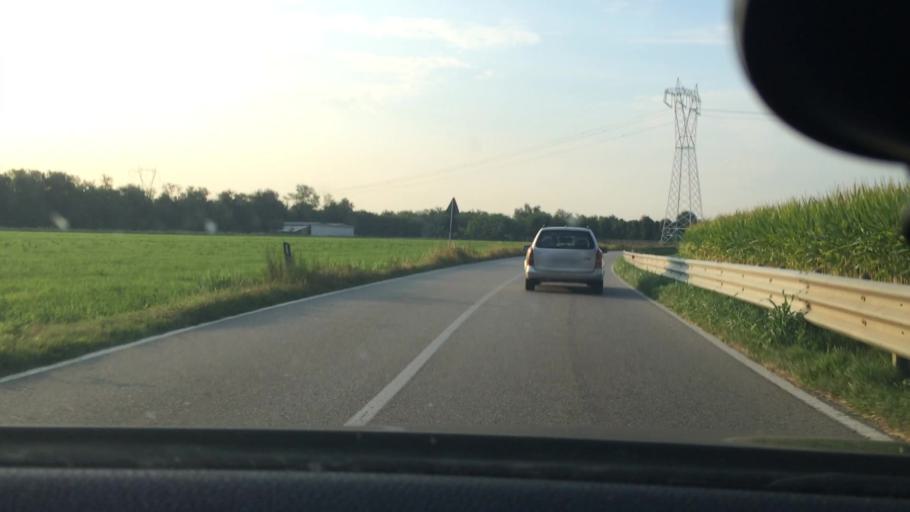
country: IT
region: Lombardy
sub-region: Citta metropolitana di Milano
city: Casorezzo
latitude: 45.5338
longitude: 8.8978
